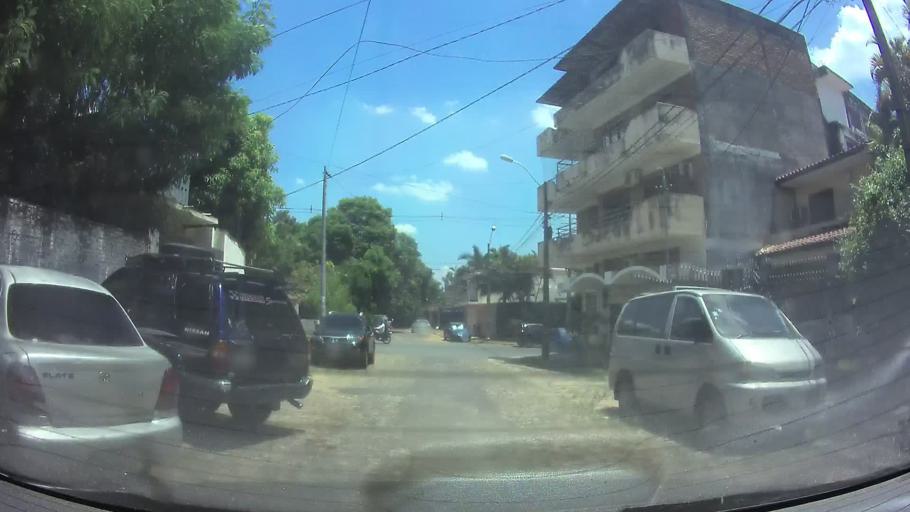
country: PY
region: Asuncion
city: Asuncion
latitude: -25.2966
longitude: -57.5893
